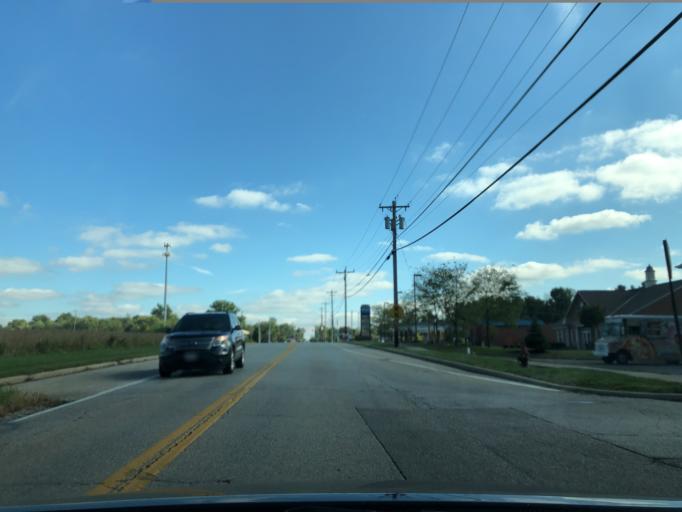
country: US
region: Ohio
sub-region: Hamilton County
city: Loveland
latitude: 39.2308
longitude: -84.2584
